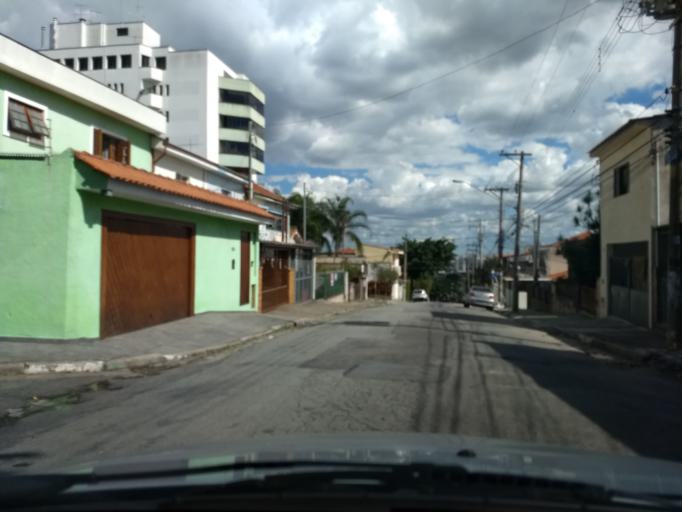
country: BR
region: Sao Paulo
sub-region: Sao Paulo
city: Sao Paulo
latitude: -23.5006
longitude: -46.5971
